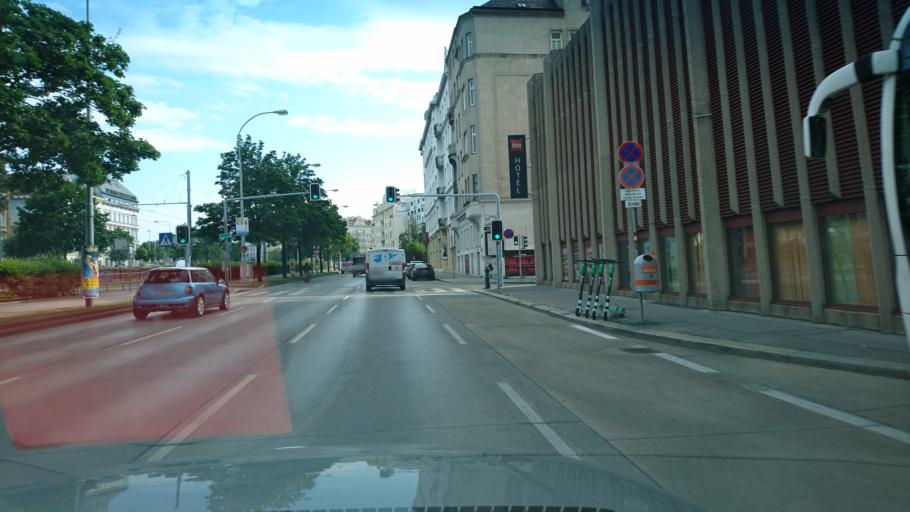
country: AT
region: Vienna
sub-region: Wien Stadt
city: Vienna
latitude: 48.1933
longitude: 16.3392
